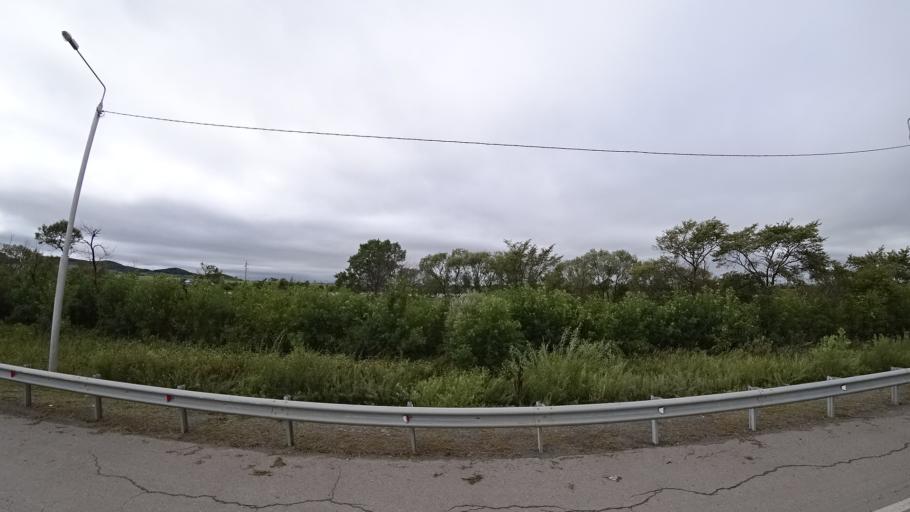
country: RU
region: Primorskiy
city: Monastyrishche
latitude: 44.1833
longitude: 132.4415
